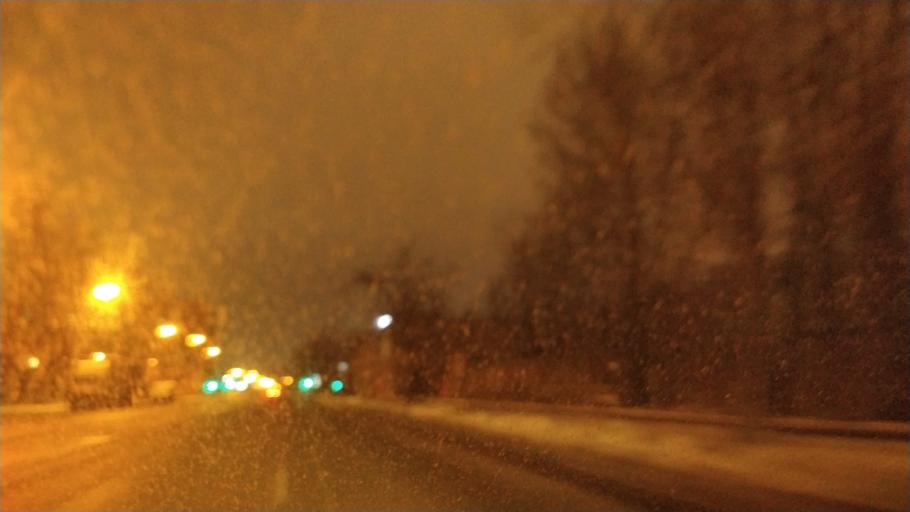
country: RU
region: St.-Petersburg
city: Kupchino
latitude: 59.8810
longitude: 30.3415
